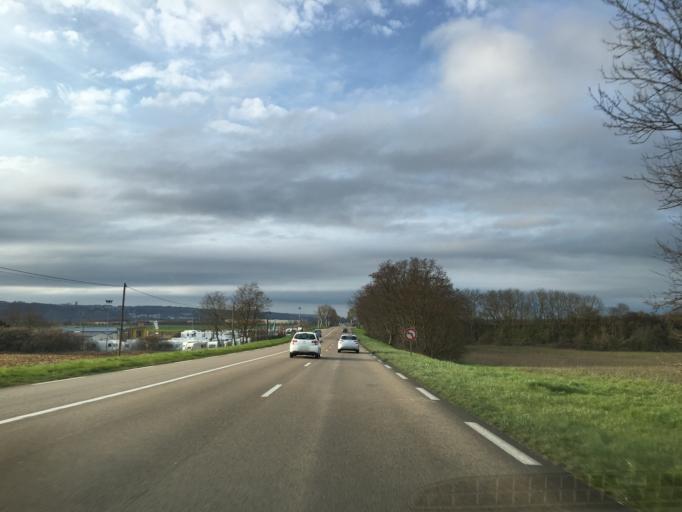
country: FR
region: Bourgogne
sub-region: Departement de l'Yonne
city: Maillot
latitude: 48.1606
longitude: 3.3029
